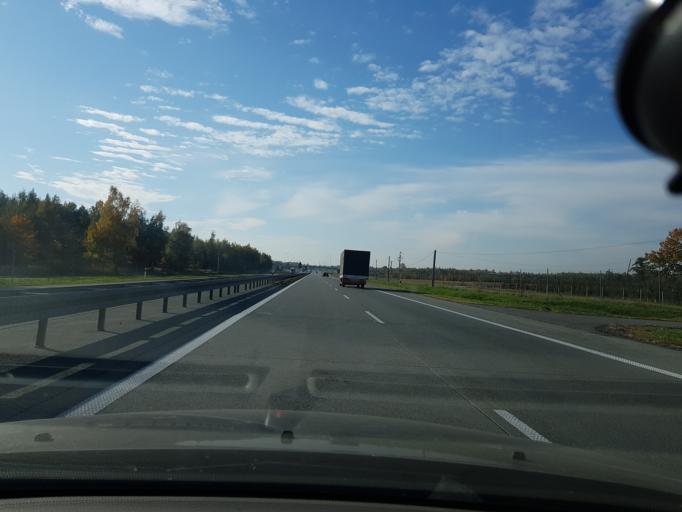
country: PL
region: Lodz Voivodeship
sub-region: Powiat skierniewicki
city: Kowiesy
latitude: 51.8729
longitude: 20.3868
